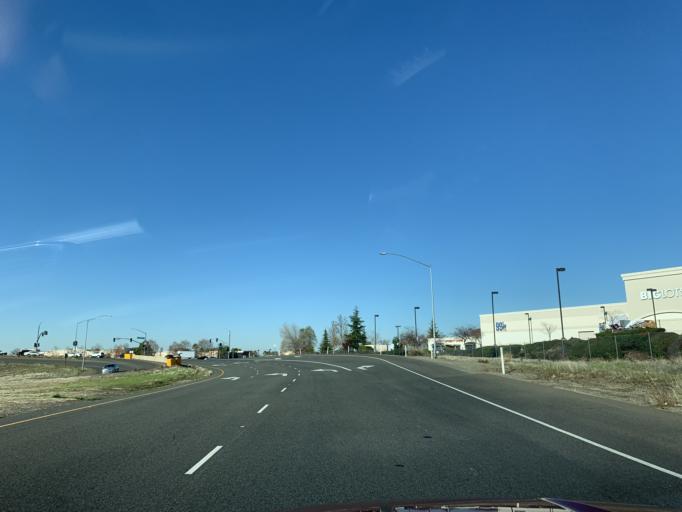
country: US
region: California
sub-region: Placer County
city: Roseville
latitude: 38.7864
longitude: -121.2817
